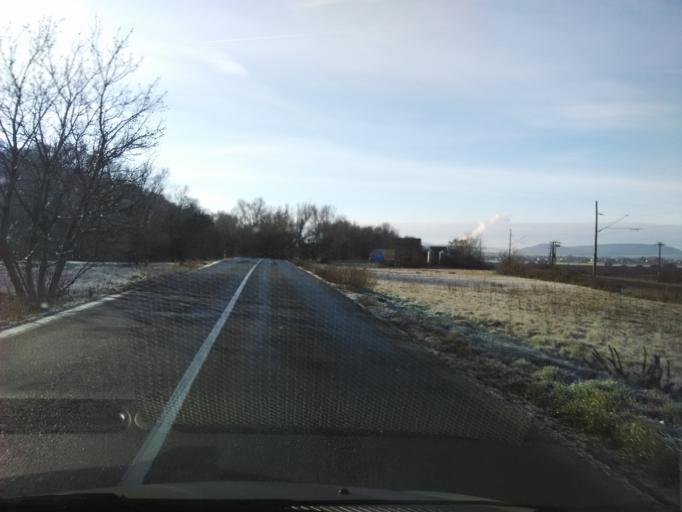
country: SK
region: Nitriansky
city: Tlmace
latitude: 48.3263
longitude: 18.5473
